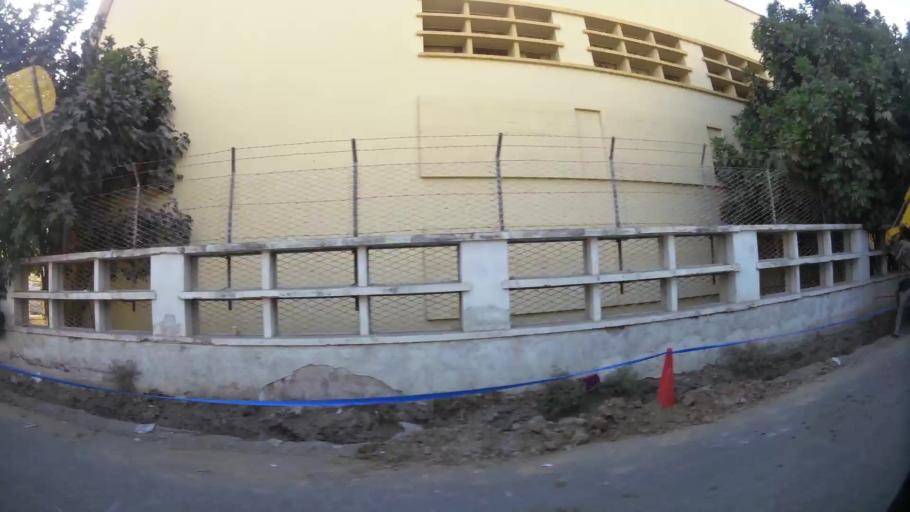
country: CY
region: Lefkosia
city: Nicosia
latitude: 35.1856
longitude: 33.3629
